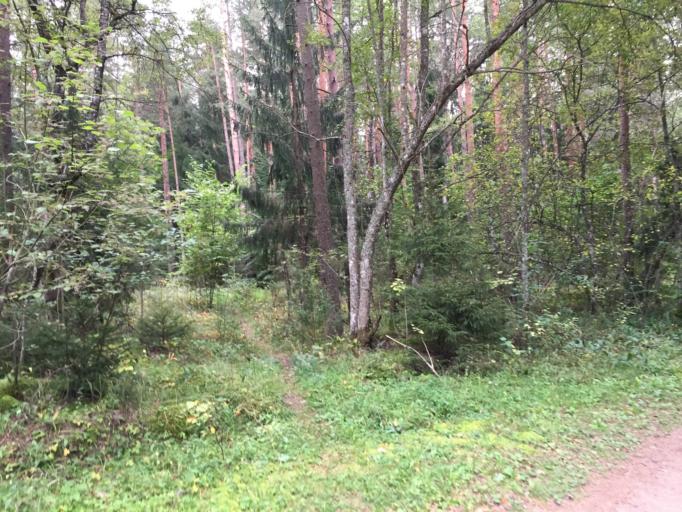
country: LV
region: Ogre
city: Ogre
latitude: 56.8367
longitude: 24.5601
